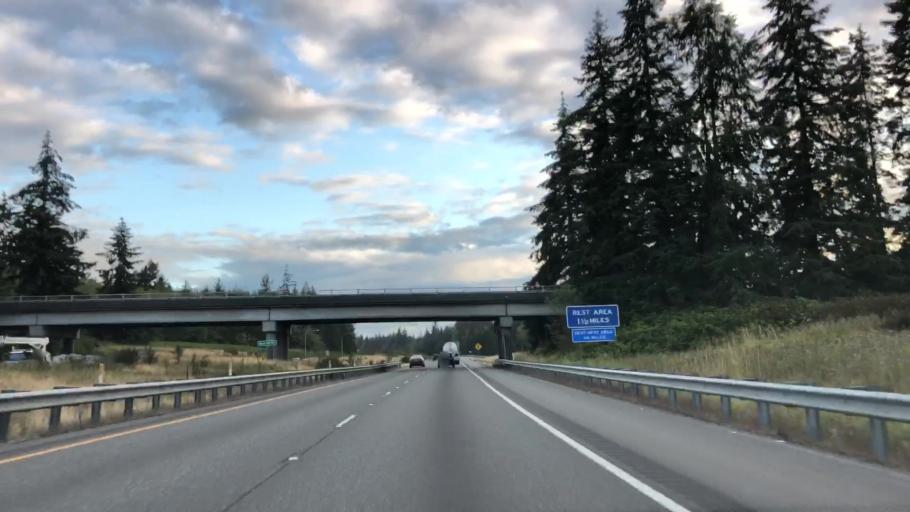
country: US
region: Washington
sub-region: Skagit County
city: Burlington
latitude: 48.5568
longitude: -122.3499
